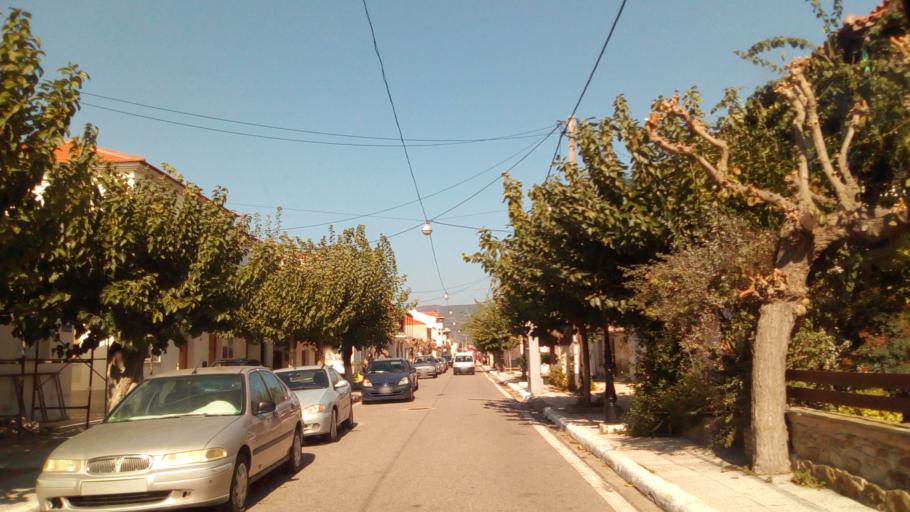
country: GR
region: West Greece
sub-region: Nomos Aitolias kai Akarnanias
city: Antirrio
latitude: 38.3299
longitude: 21.7646
